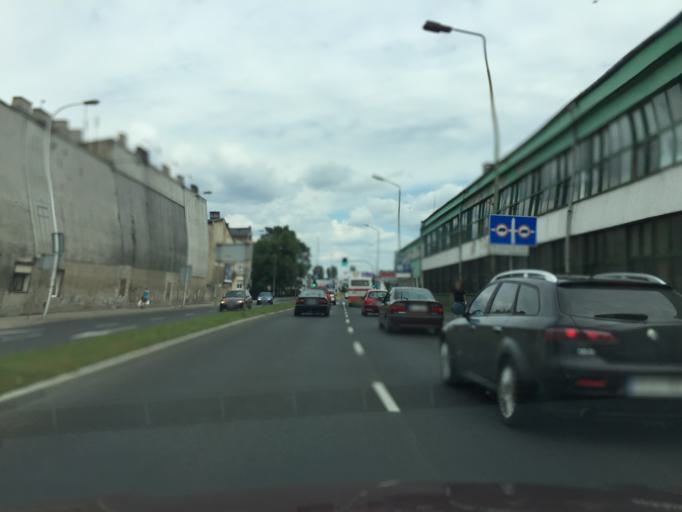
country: PL
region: Greater Poland Voivodeship
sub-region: Kalisz
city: Kalisz
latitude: 51.7656
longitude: 18.0803
